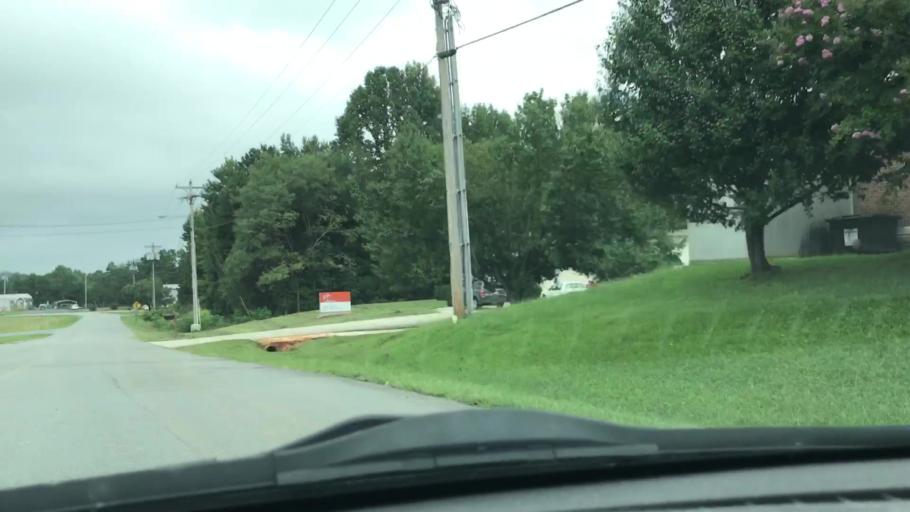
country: US
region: North Carolina
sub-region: Randolph County
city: Randleman
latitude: 35.8010
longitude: -79.8111
